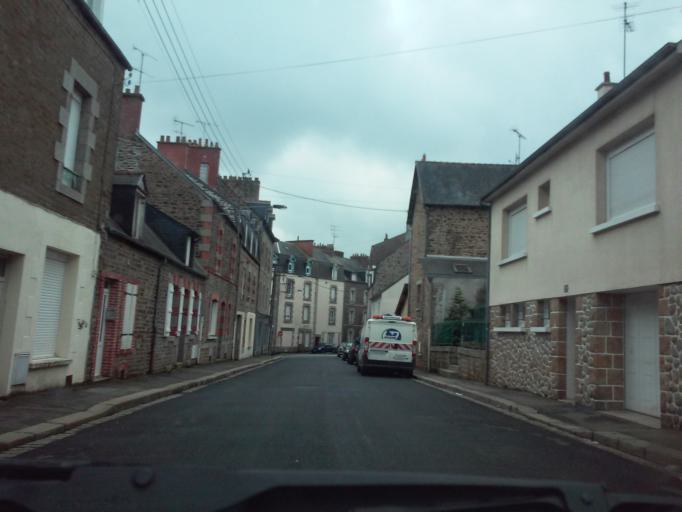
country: FR
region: Brittany
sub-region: Departement d'Ille-et-Vilaine
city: Fougeres
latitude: 48.3568
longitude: -1.1934
